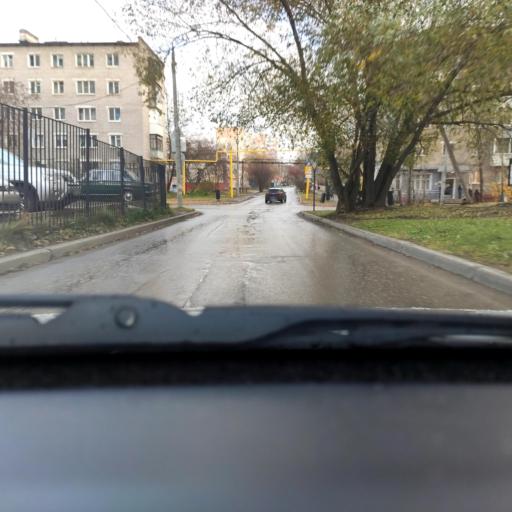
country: RU
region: Perm
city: Kondratovo
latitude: 58.0384
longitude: 56.1247
